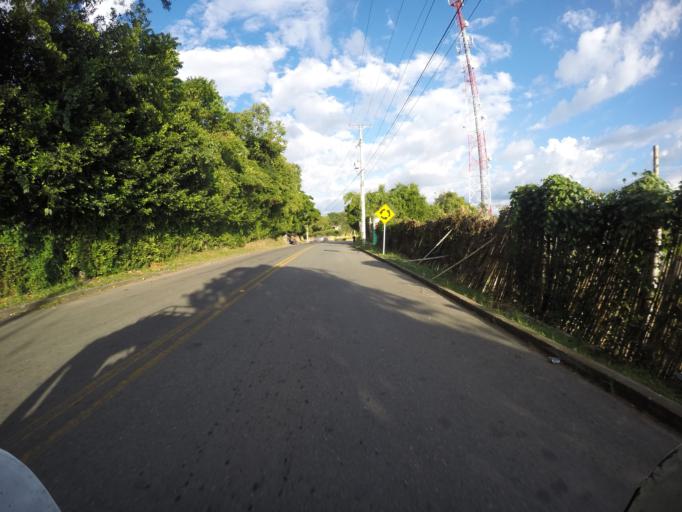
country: CO
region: Valle del Cauca
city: Alcala
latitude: 4.6773
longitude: -75.7892
